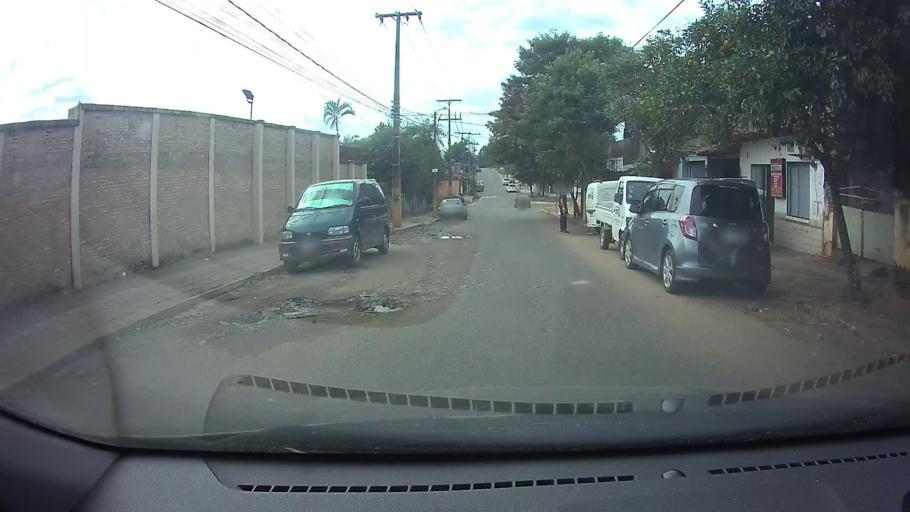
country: PY
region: Central
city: Fernando de la Mora
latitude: -25.3058
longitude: -57.5309
